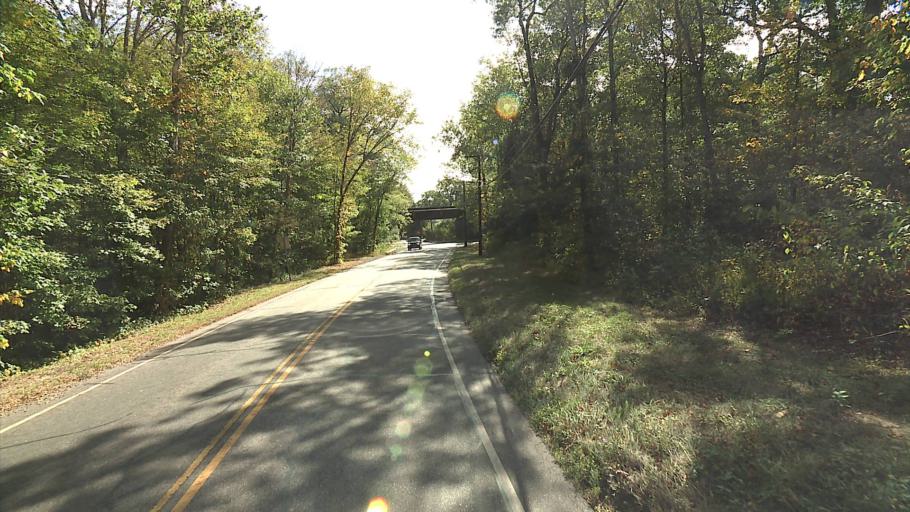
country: US
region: Connecticut
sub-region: Middlesex County
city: Durham
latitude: 41.5099
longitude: -72.7182
